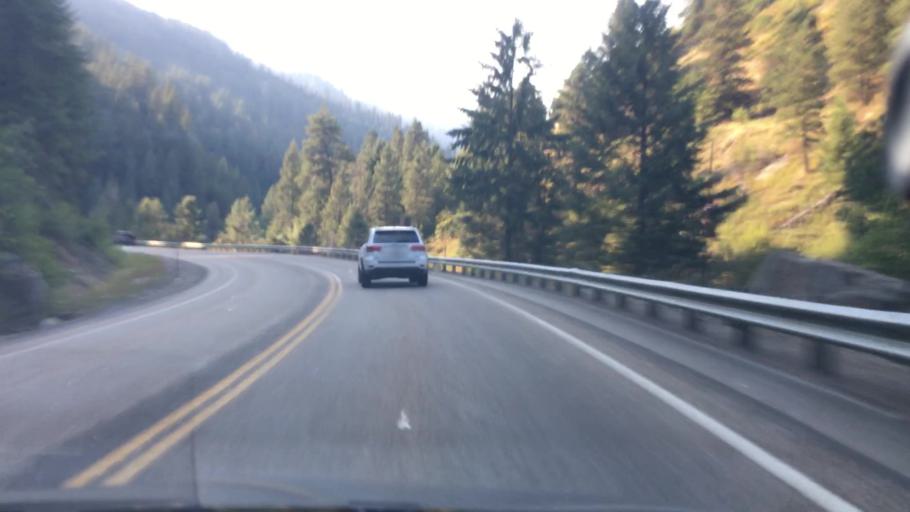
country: US
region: Idaho
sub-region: Valley County
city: Cascade
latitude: 44.1500
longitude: -116.1123
